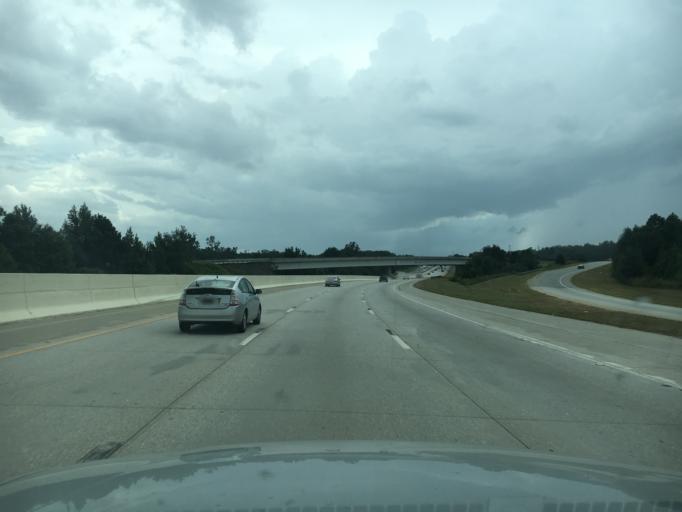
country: US
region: South Carolina
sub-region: Greenville County
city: Mauldin
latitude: 34.7697
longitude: -82.2739
